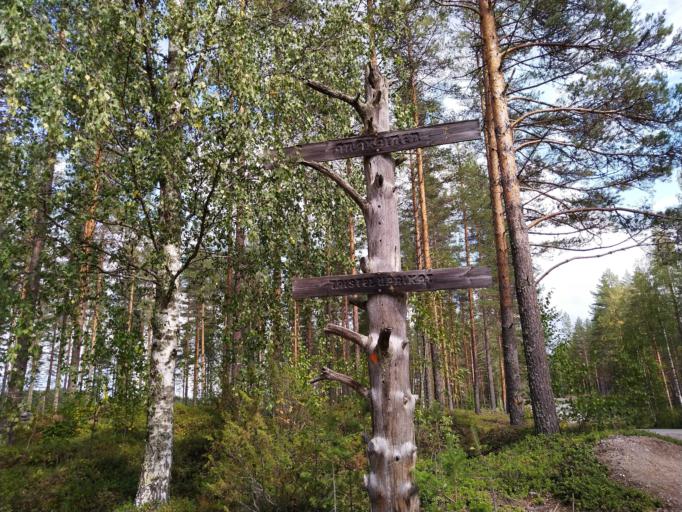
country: FI
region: North Karelia
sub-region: Pielisen Karjala
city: Lieksa
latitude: 63.5689
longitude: 30.0979
